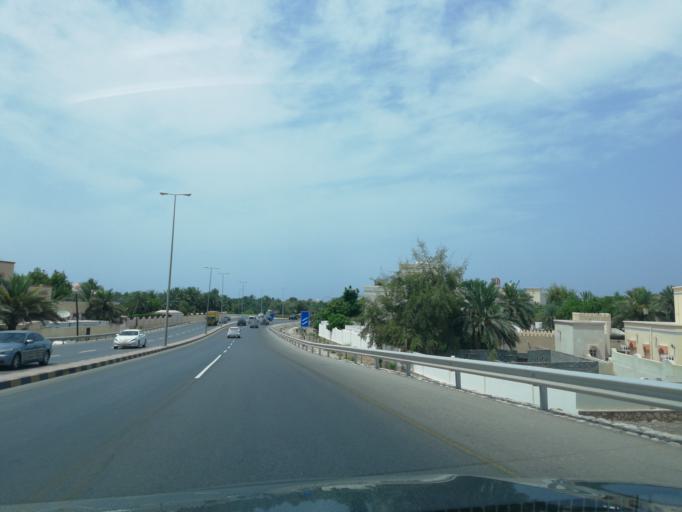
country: OM
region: Muhafazat Masqat
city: As Sib al Jadidah
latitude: 23.6768
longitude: 58.1388
